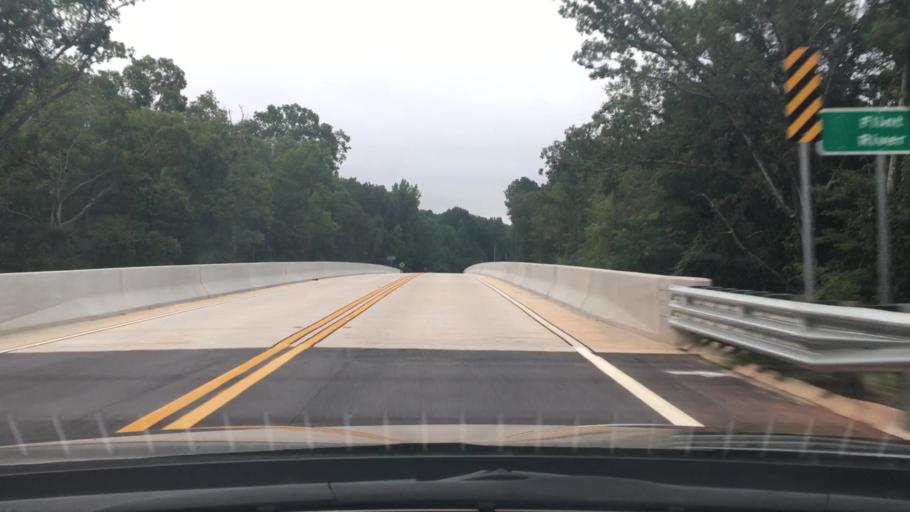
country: US
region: Georgia
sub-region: Fayette County
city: Shannon
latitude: 33.2828
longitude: -84.4252
